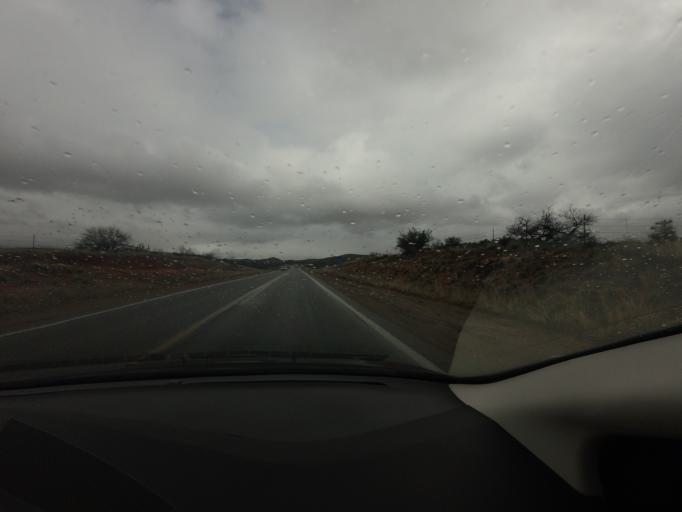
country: US
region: Arizona
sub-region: Yavapai County
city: Cornville
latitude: 34.7118
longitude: -111.8807
